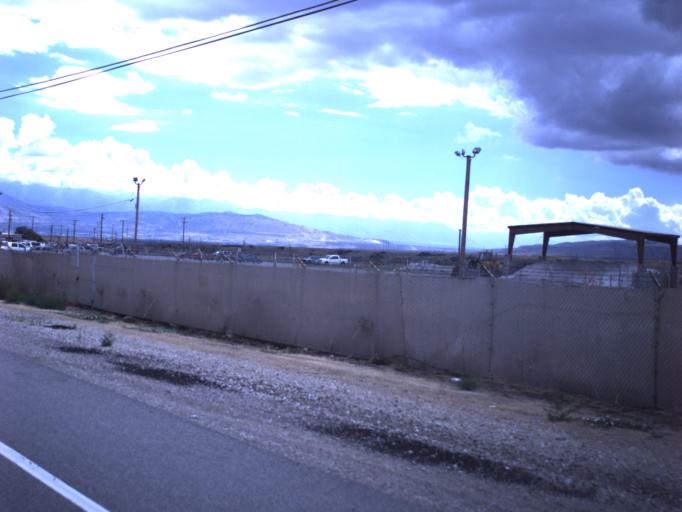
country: US
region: Utah
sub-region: Salt Lake County
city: Herriman
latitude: 40.5661
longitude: -112.0866
